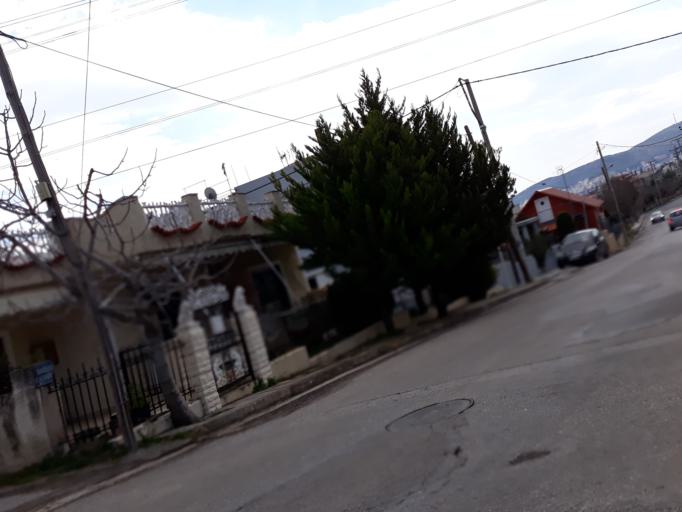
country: GR
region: Attica
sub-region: Nomarchia Dytikis Attikis
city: Ano Liosia
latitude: 38.0926
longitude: 23.7107
